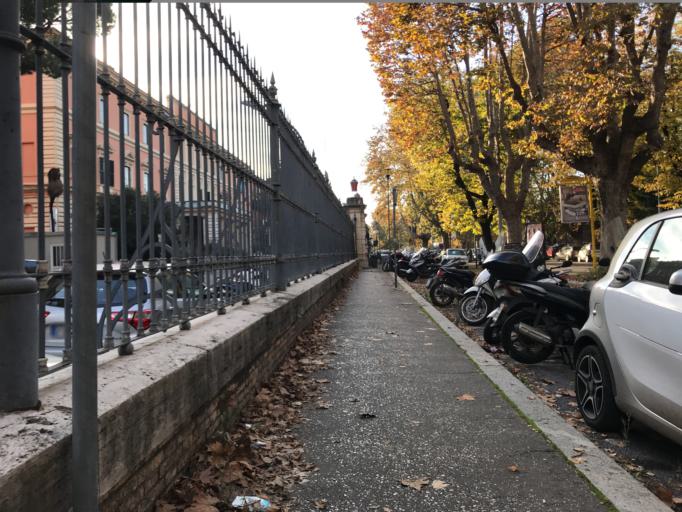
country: IT
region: Latium
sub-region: Citta metropolitana di Roma Capitale
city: Rome
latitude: 41.9073
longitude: 12.5094
